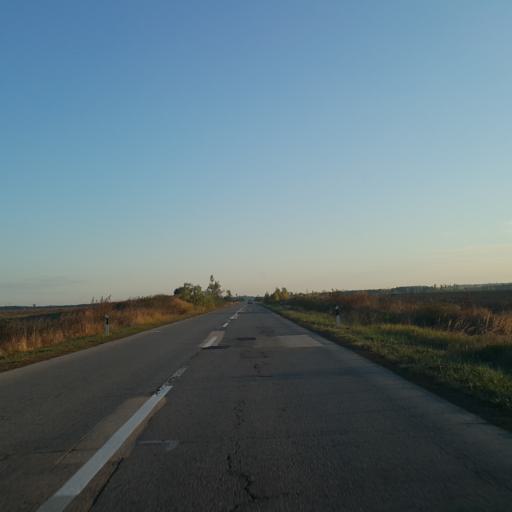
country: RS
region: Central Serbia
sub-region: Borski Okrug
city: Negotin
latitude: 44.1311
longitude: 22.3443
